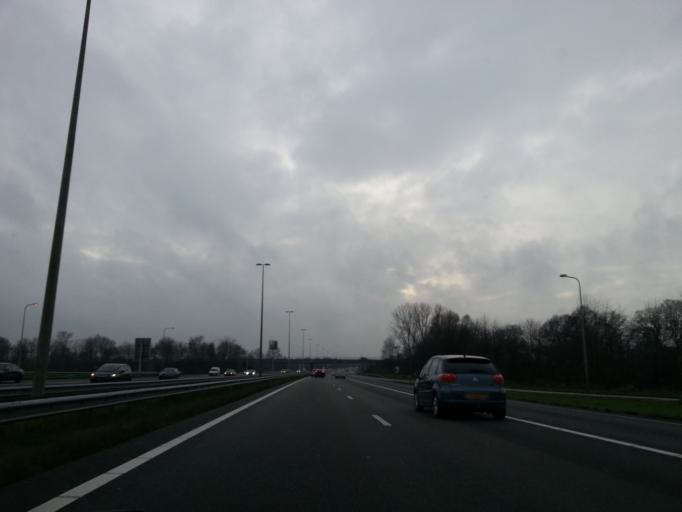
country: NL
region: Gelderland
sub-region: Gemeente Apeldoorn
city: Loenen
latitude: 52.1666
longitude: 6.0248
